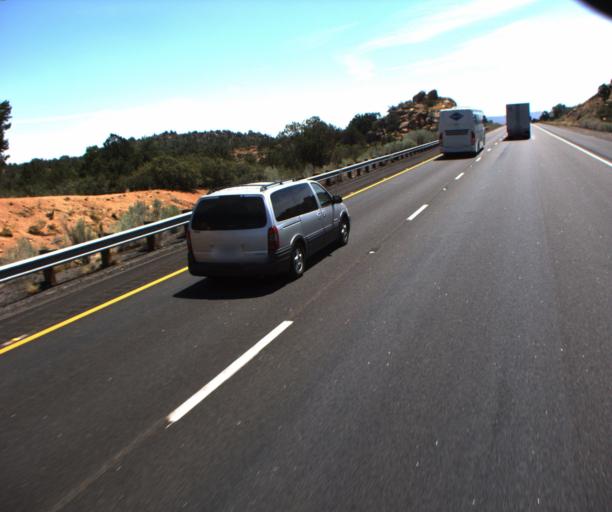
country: US
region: Arizona
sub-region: Mohave County
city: Peach Springs
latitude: 35.1843
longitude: -113.3987
